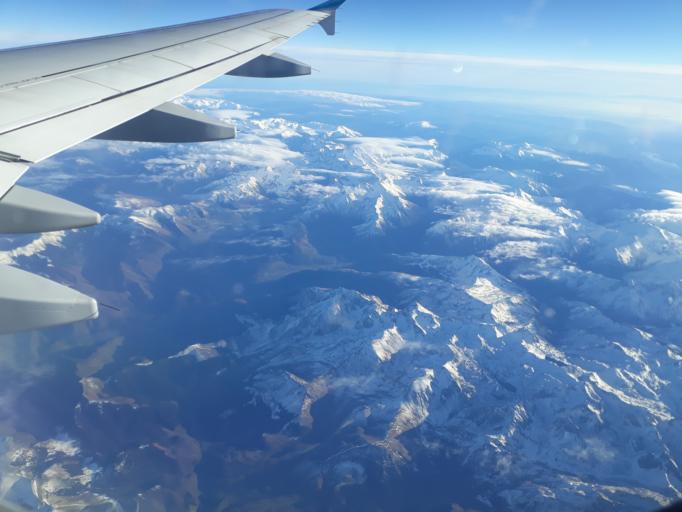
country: FR
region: Midi-Pyrenees
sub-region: Departement des Hautes-Pyrenees
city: Campan
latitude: 43.0182
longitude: 0.1698
